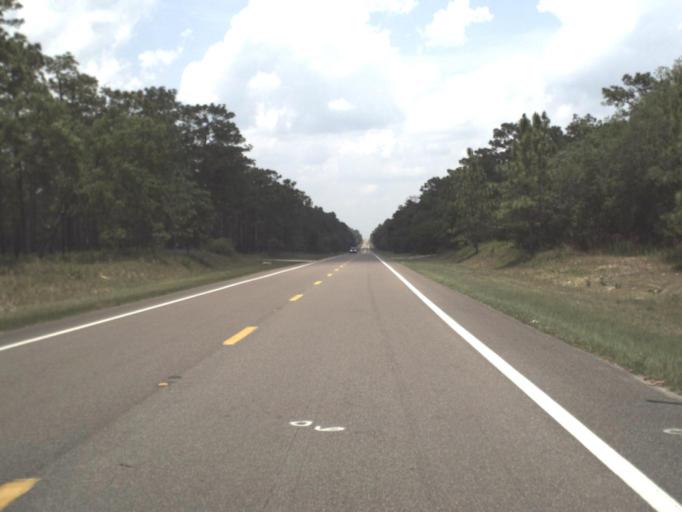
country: US
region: Florida
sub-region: Putnam County
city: Crescent City
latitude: 29.4083
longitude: -81.7369
